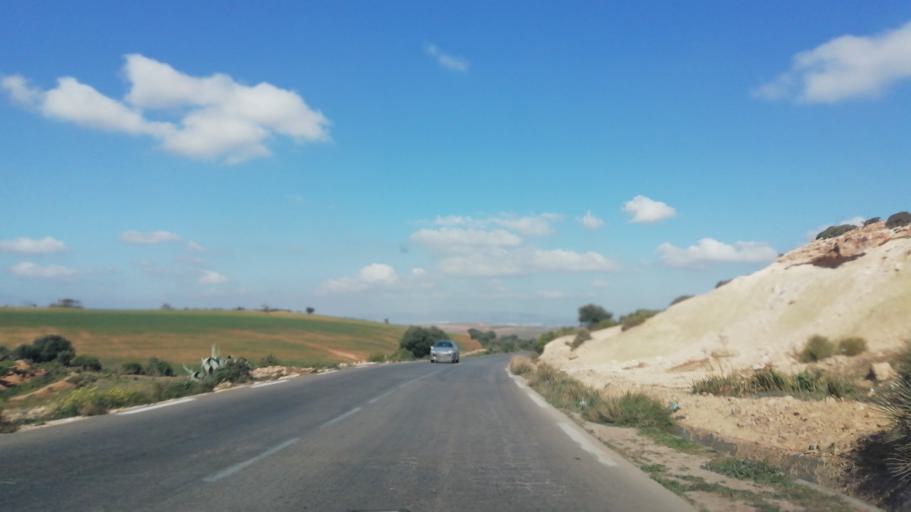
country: DZ
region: Oran
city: Ain el Bya
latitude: 35.7233
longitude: -0.2441
